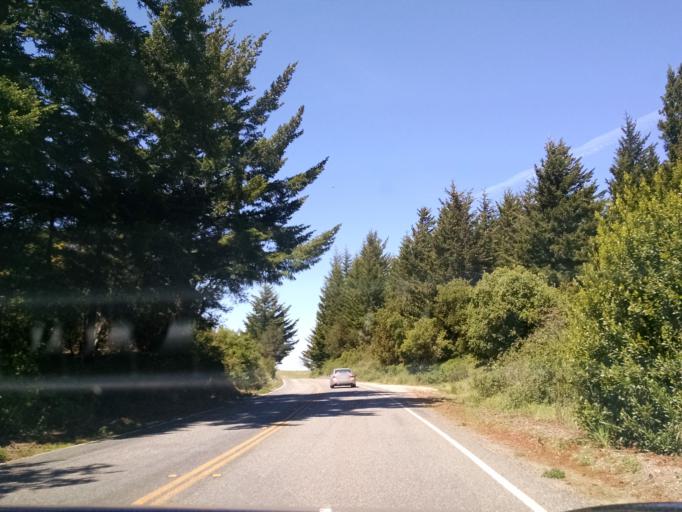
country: US
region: California
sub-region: San Mateo County
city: Portola Valley
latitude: 37.3491
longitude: -122.2331
